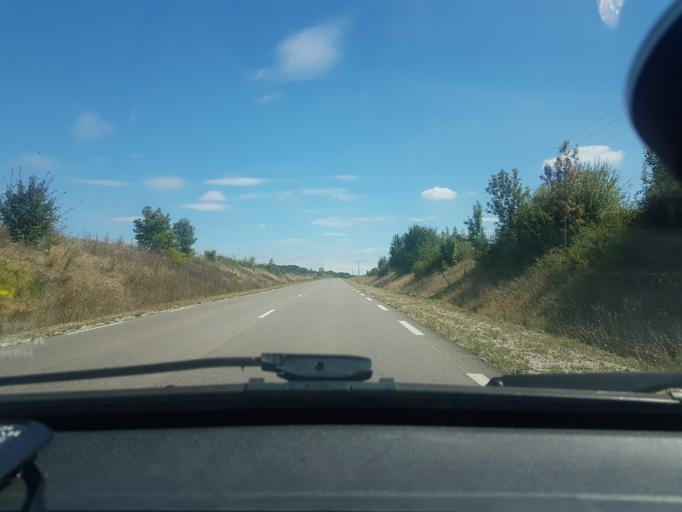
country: FR
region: Franche-Comte
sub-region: Departement de la Haute-Saone
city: Gray-la-Ville
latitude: 47.4049
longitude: 5.4835
